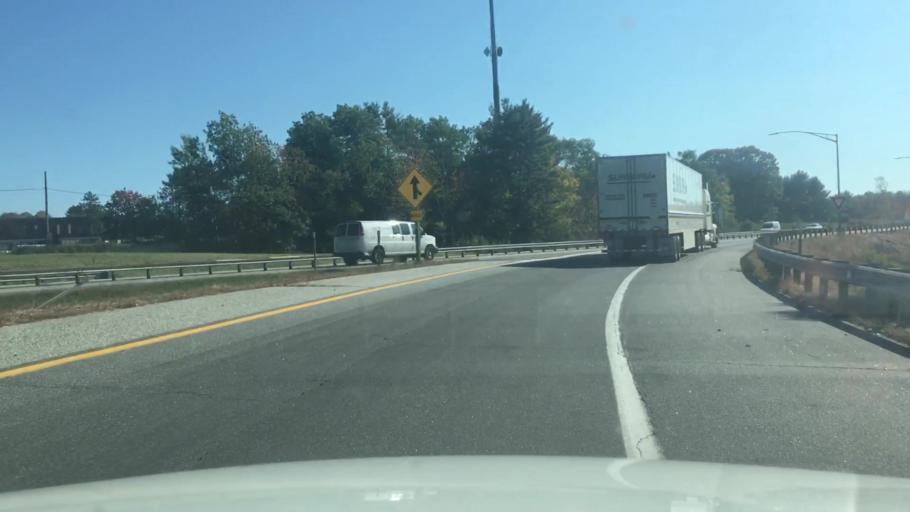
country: US
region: Maine
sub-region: Cumberland County
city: Falmouth
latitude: 43.7184
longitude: -70.3062
